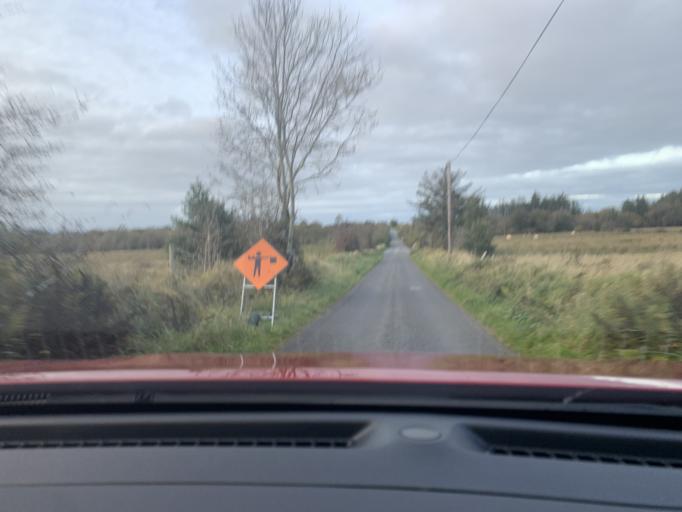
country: IE
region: Connaught
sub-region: Roscommon
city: Ballaghaderreen
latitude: 53.9795
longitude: -8.6173
